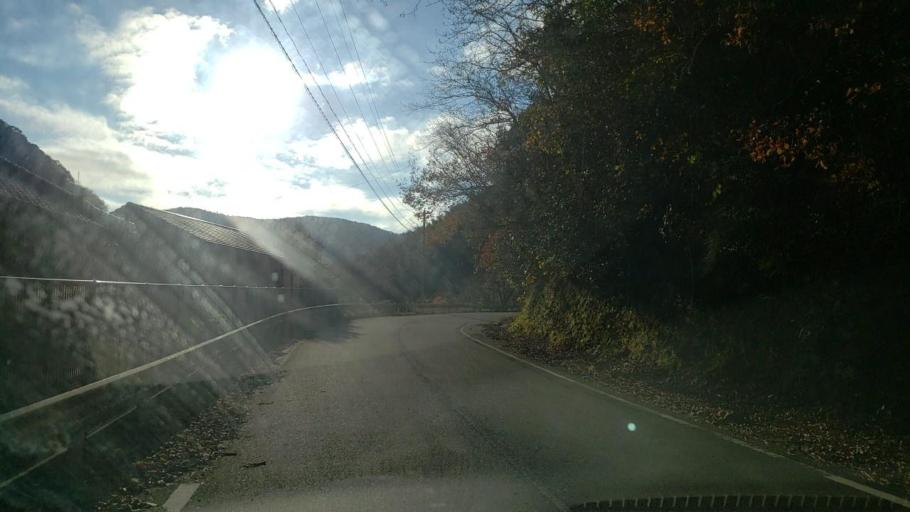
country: JP
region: Tokushima
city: Wakimachi
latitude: 34.1008
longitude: 134.0732
